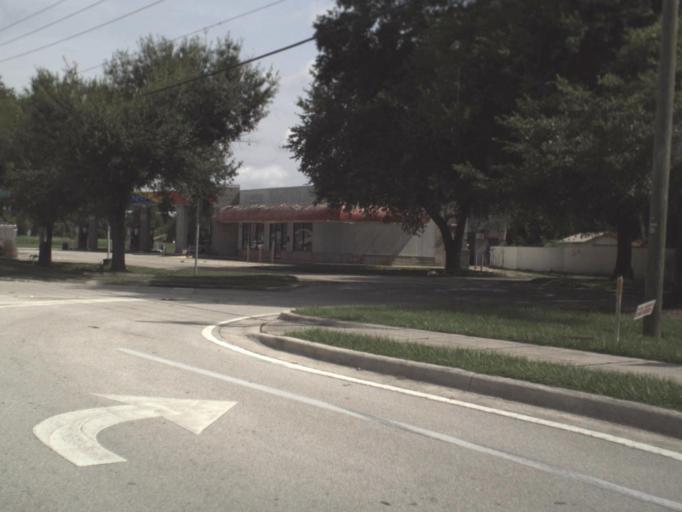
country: US
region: Florida
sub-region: Polk County
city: Jan-Phyl Village
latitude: 28.0067
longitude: -81.7513
